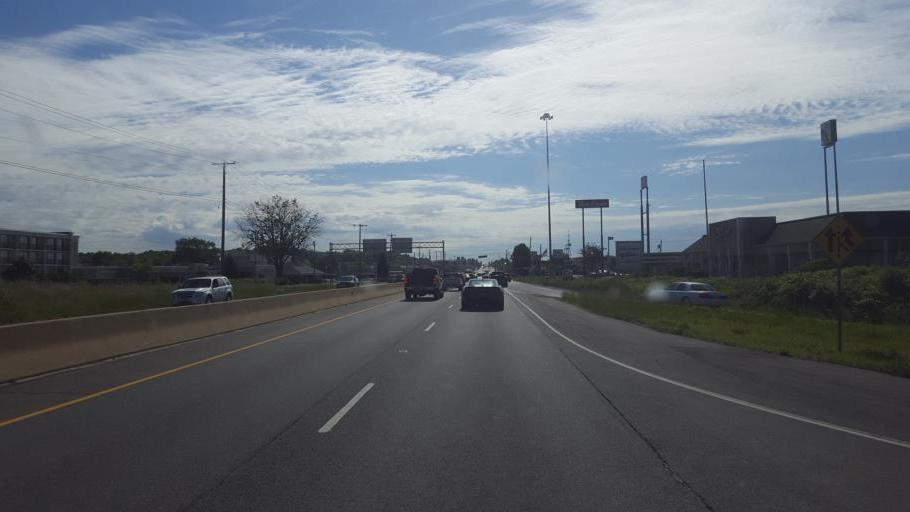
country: US
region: Ohio
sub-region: Summit County
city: Montrose-Ghent
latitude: 41.1359
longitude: -81.6483
